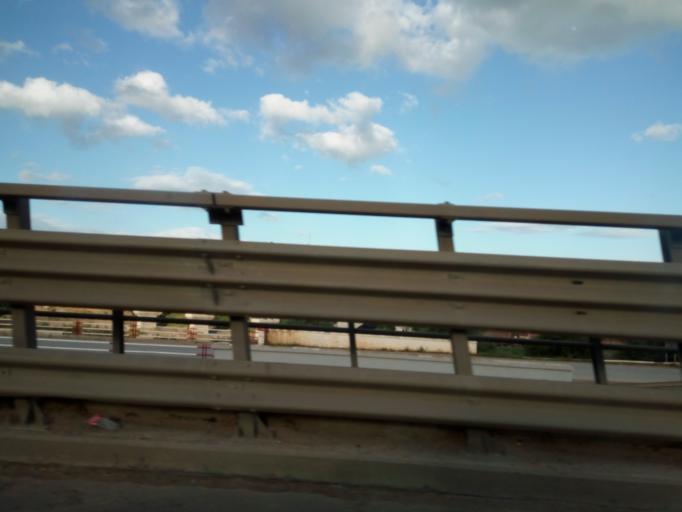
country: DZ
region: Tipaza
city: Hadjout
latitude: 36.3721
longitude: 2.4639
